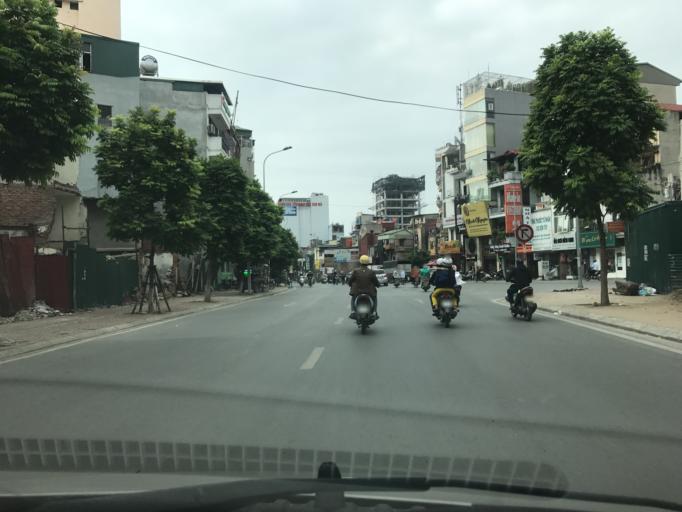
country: VN
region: Ha Noi
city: Dong Da
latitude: 21.0326
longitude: 105.8309
